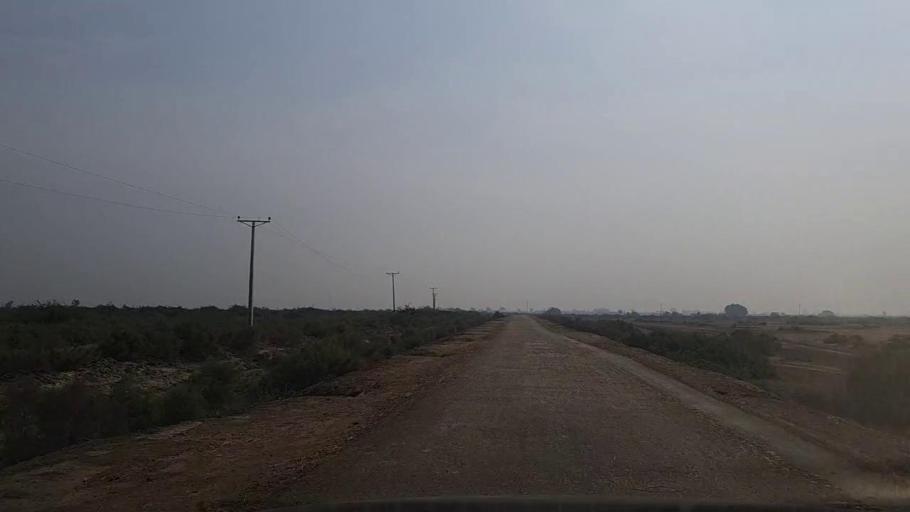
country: PK
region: Sindh
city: Mirpur Sakro
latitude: 24.3881
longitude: 67.7523
